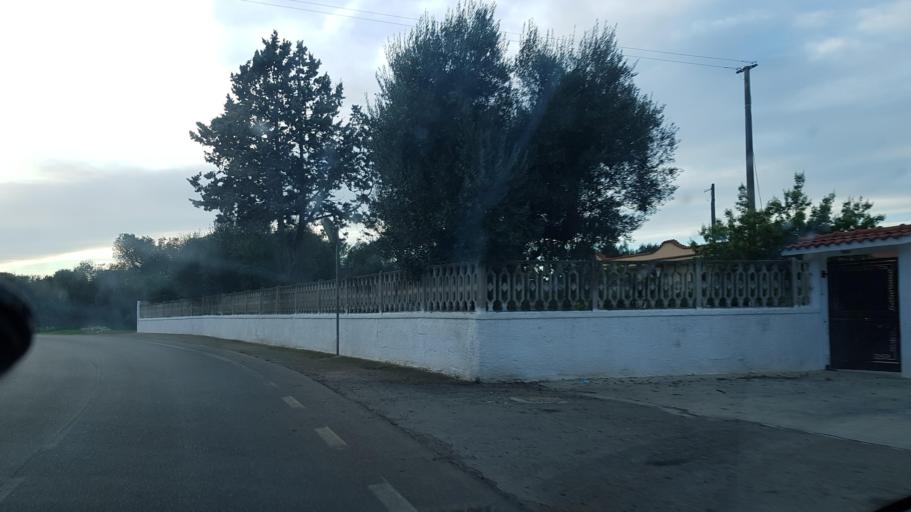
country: IT
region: Apulia
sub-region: Provincia di Brindisi
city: San Vito dei Normanni
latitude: 40.6495
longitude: 17.6880
